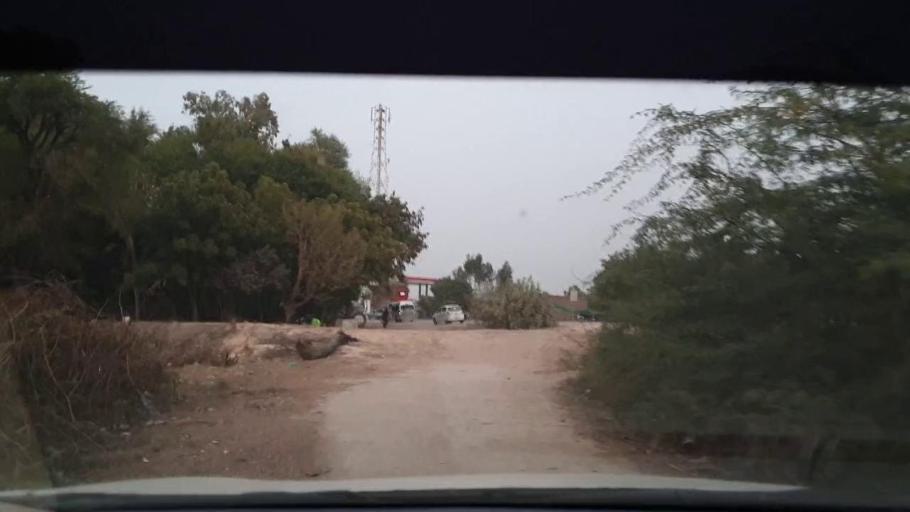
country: PK
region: Sindh
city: Berani
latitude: 25.8446
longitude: 68.7905
